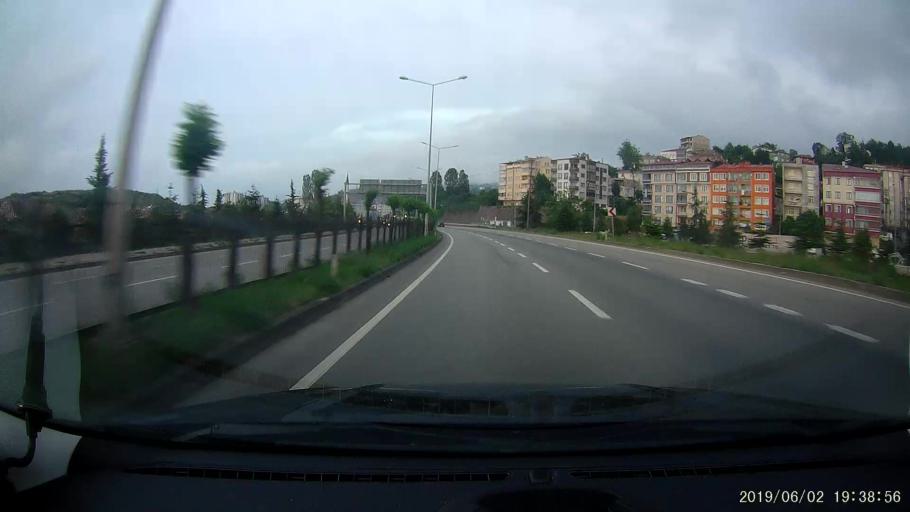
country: TR
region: Giresun
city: Giresun
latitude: 40.9118
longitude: 38.4310
